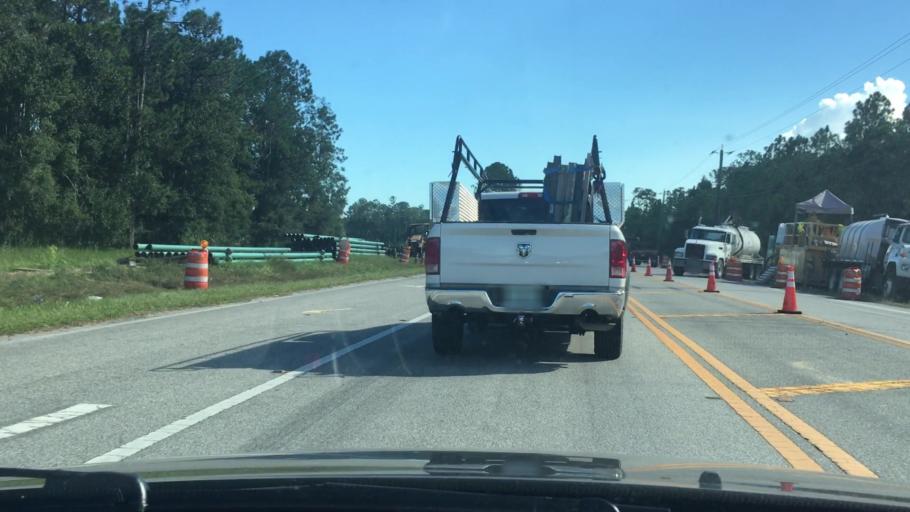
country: US
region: Florida
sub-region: Volusia County
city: Samsula-Spruce Creek
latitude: 29.1105
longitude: -81.0699
